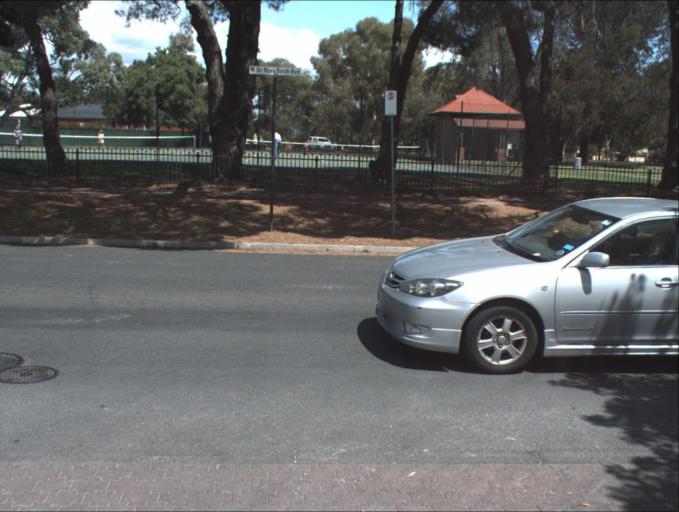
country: AU
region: South Australia
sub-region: Port Adelaide Enfield
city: Gilles Plains
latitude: -34.8565
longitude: 138.6394
